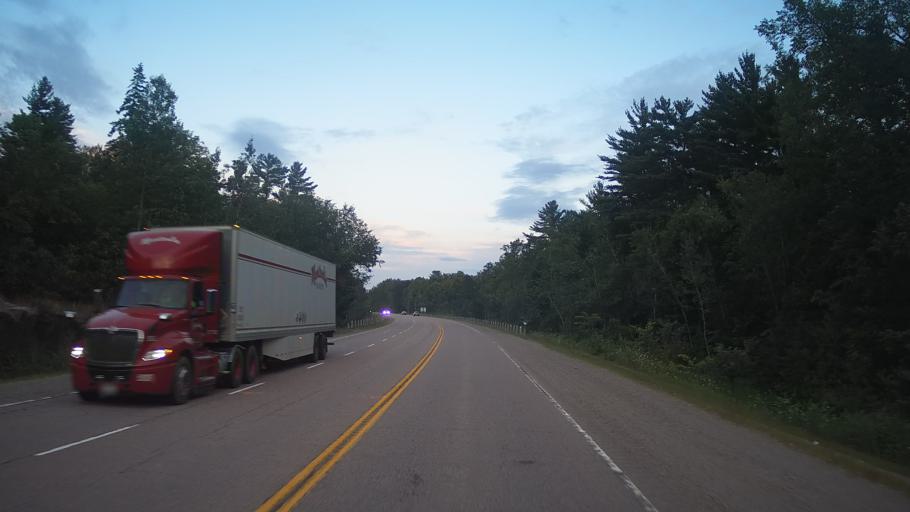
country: CA
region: Ontario
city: Pembroke
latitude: 45.7524
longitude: -77.0253
